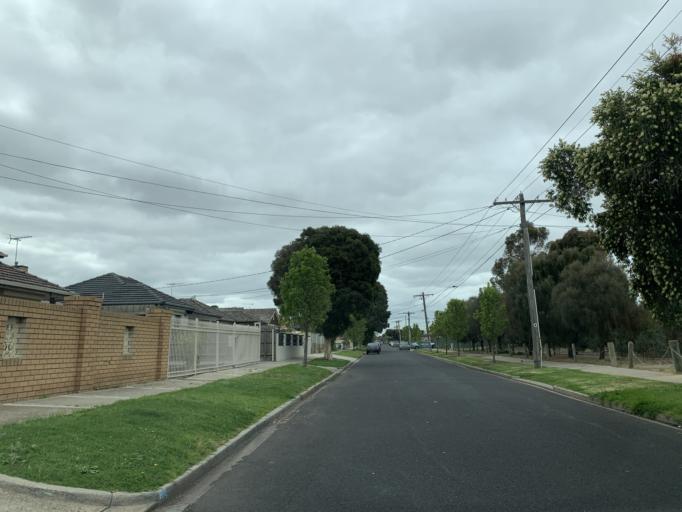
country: AU
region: Victoria
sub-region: Brimbank
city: St Albans
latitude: -37.7399
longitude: 144.8084
